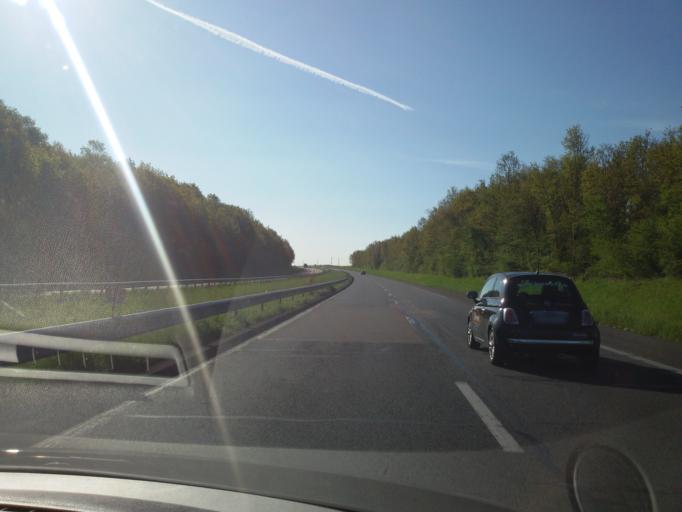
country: FR
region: Ile-de-France
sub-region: Departement de Seine-et-Marne
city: Egreville
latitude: 48.1398
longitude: 2.9146
